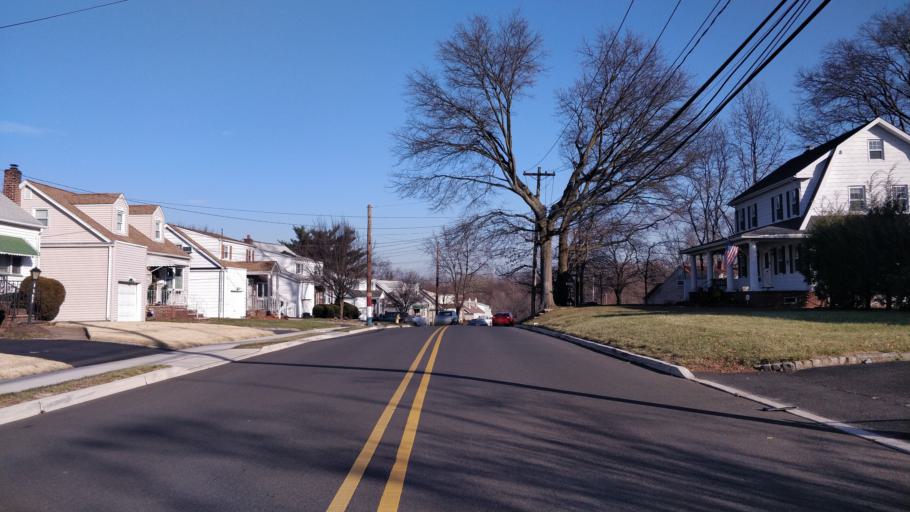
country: US
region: New Jersey
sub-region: Union County
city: Union
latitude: 40.7028
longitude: -74.2557
